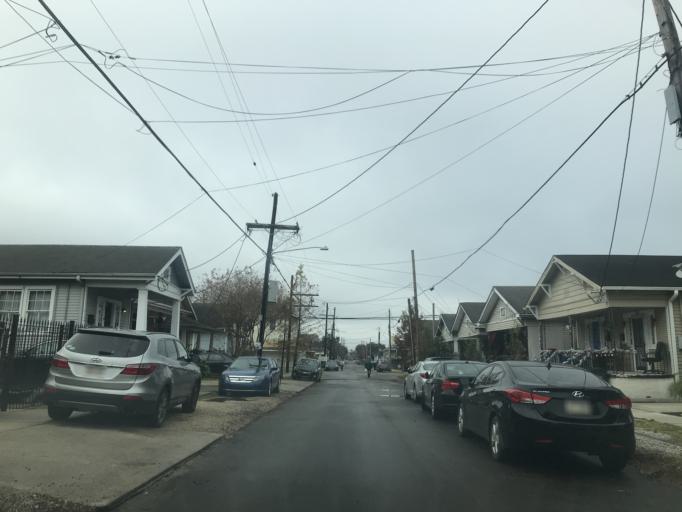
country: US
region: Louisiana
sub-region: Orleans Parish
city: New Orleans
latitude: 29.9710
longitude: -90.1056
